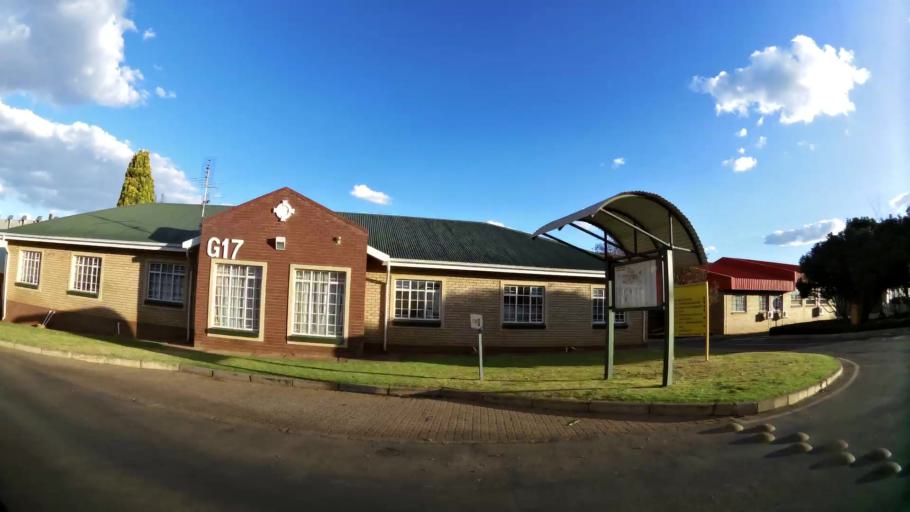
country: ZA
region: North-West
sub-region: Dr Kenneth Kaunda District Municipality
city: Potchefstroom
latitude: -26.6840
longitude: 27.0935
